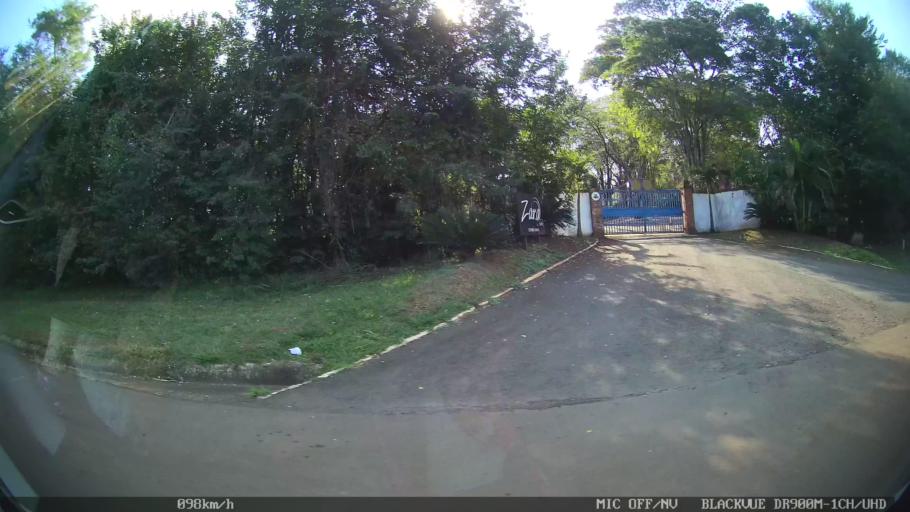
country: BR
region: Sao Paulo
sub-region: Piracicaba
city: Piracicaba
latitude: -22.6981
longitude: -47.5931
